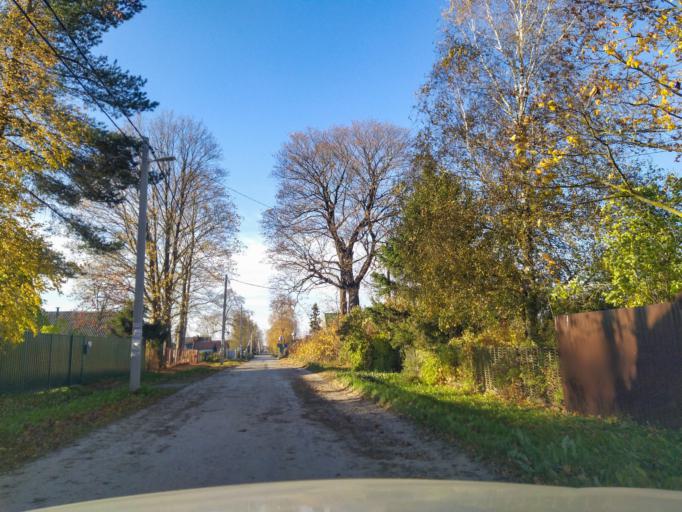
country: RU
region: Leningrad
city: Siverskiy
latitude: 59.3265
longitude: 30.0408
